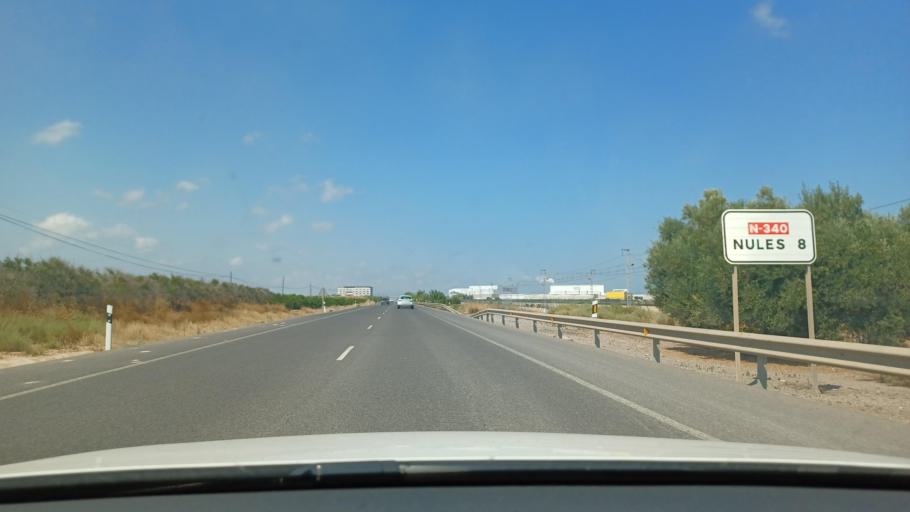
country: ES
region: Valencia
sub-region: Provincia de Castello
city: Chilches
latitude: 39.7867
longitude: -0.1875
